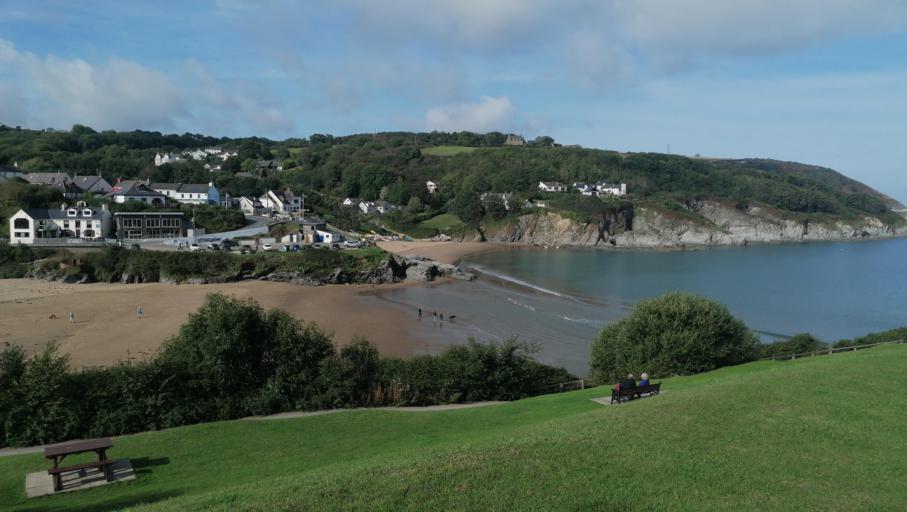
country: GB
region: Wales
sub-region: County of Ceredigion
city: Aberporth
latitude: 52.1347
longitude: -4.5434
